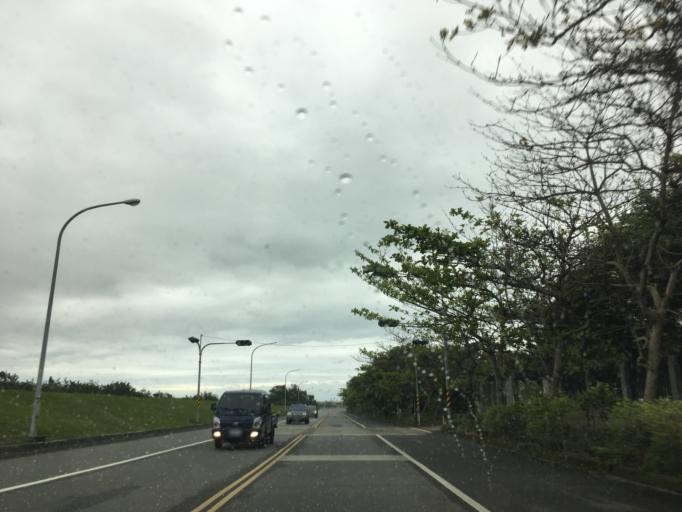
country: TW
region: Taiwan
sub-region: Hualien
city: Hualian
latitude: 24.0020
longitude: 121.5738
